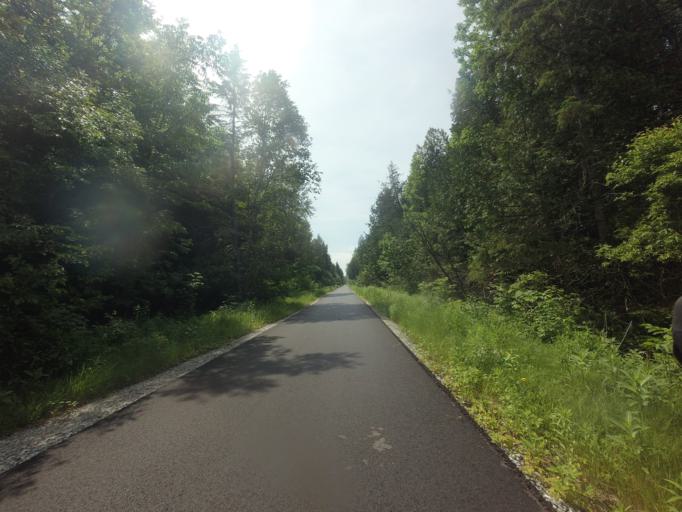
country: CA
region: Quebec
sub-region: Outaouais
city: Maniwaki
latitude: 46.1779
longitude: -76.0420
